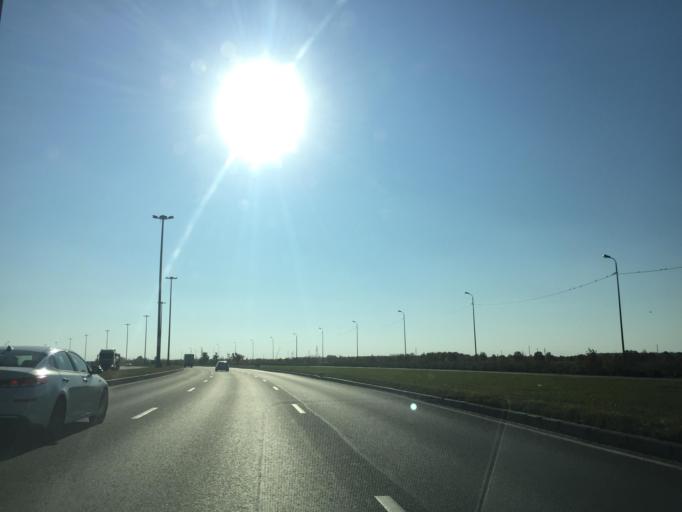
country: RU
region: St.-Petersburg
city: Petro-Slavyanka
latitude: 59.7683
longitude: 30.5008
